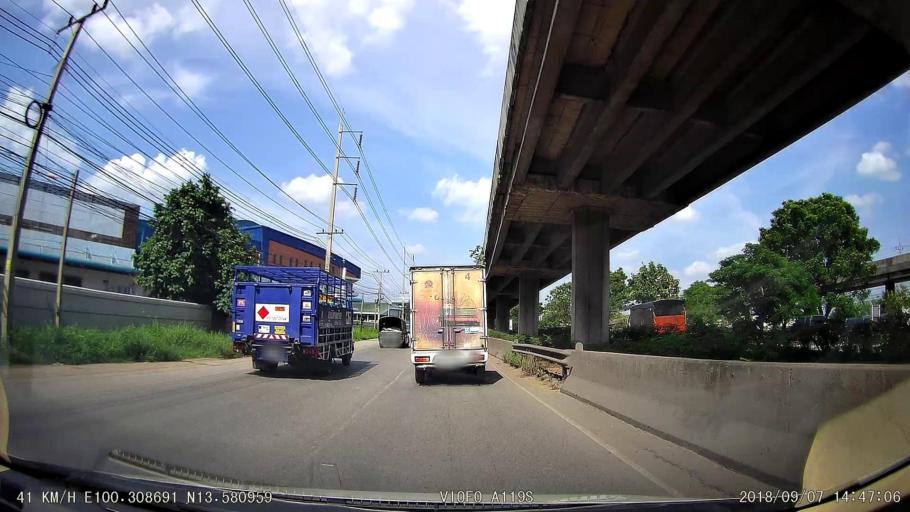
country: TH
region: Samut Sakhon
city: Samut Sakhon
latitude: 13.5810
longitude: 100.3088
